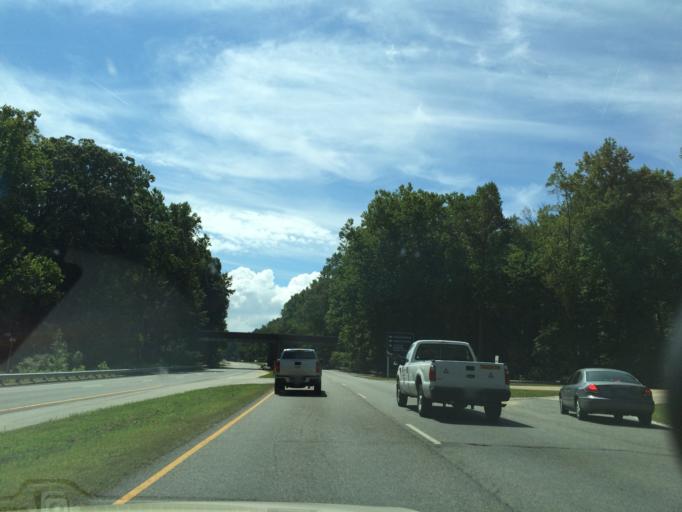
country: US
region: Virginia
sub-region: York County
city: Yorktown
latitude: 37.2303
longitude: -76.5147
